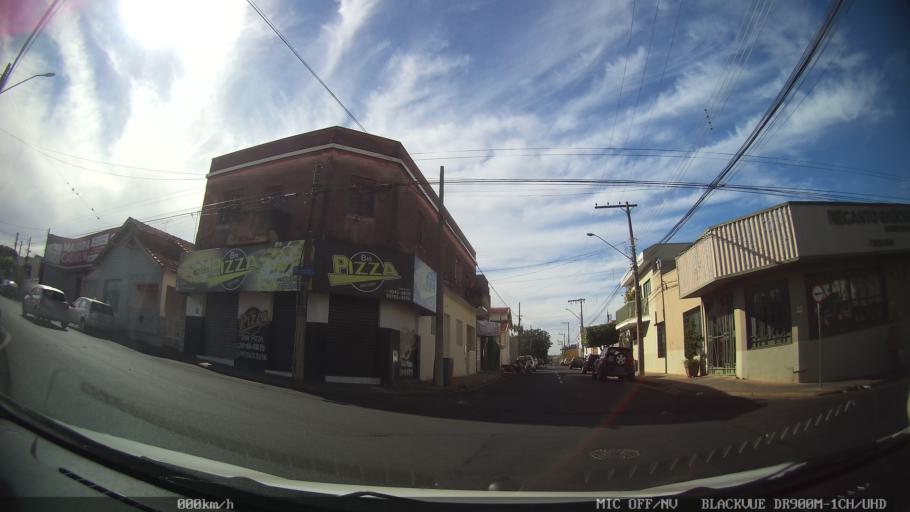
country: BR
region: Sao Paulo
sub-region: Catanduva
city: Catanduva
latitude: -21.1269
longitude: -48.9679
